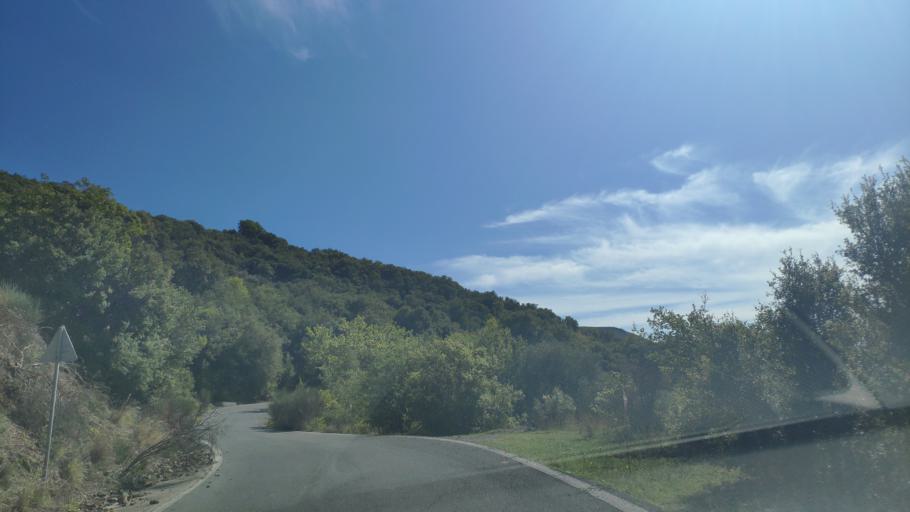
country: GR
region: Peloponnese
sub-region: Nomos Arkadias
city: Dimitsana
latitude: 37.5373
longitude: 22.0481
